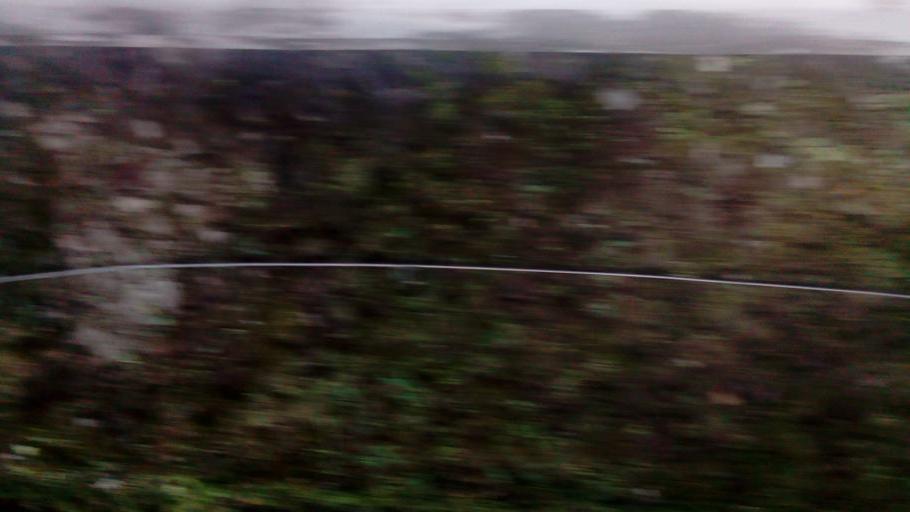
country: TW
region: Taiwan
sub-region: Yilan
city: Yilan
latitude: 24.5709
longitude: 121.4731
